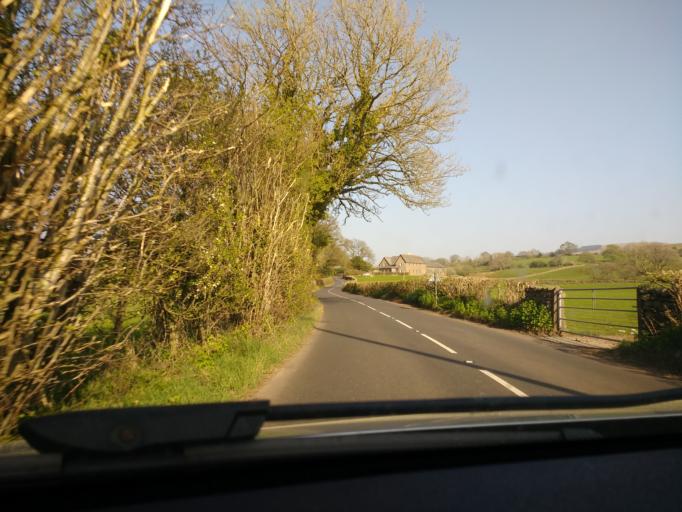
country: GB
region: England
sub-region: Cumbria
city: Sedbergh
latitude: 54.3202
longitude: -2.5050
